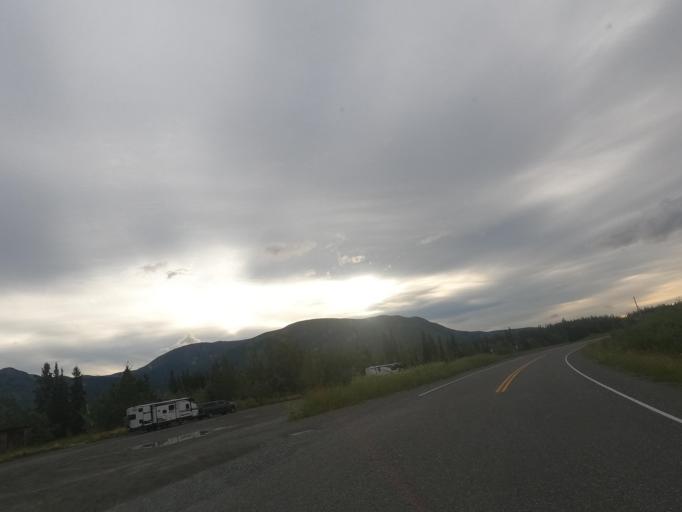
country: CA
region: Yukon
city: Haines Junction
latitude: 60.8588
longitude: -137.0618
